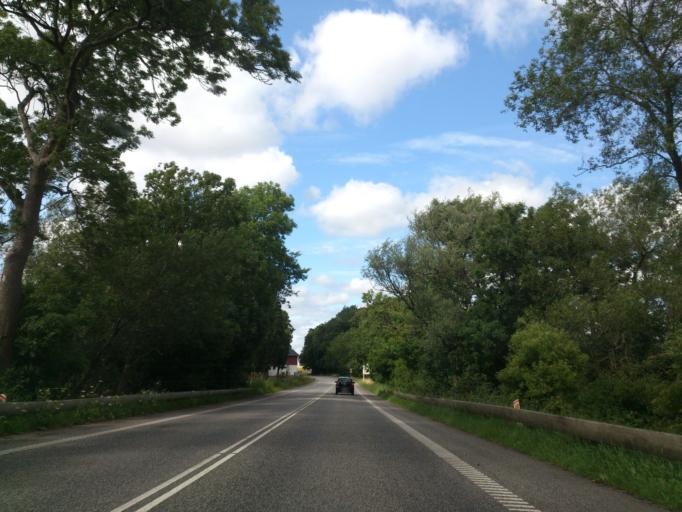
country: DK
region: South Denmark
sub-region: Aabenraa Kommune
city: Krusa
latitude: 54.9398
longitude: 9.4522
